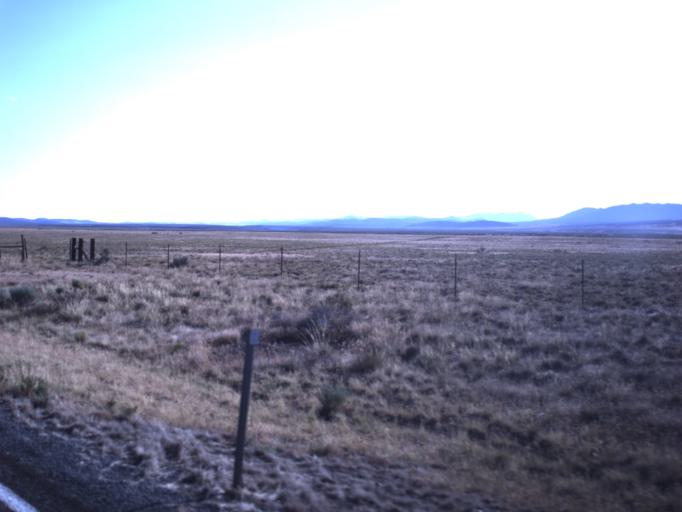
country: US
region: Utah
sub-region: Iron County
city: Enoch
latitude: 37.8933
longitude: -113.0316
